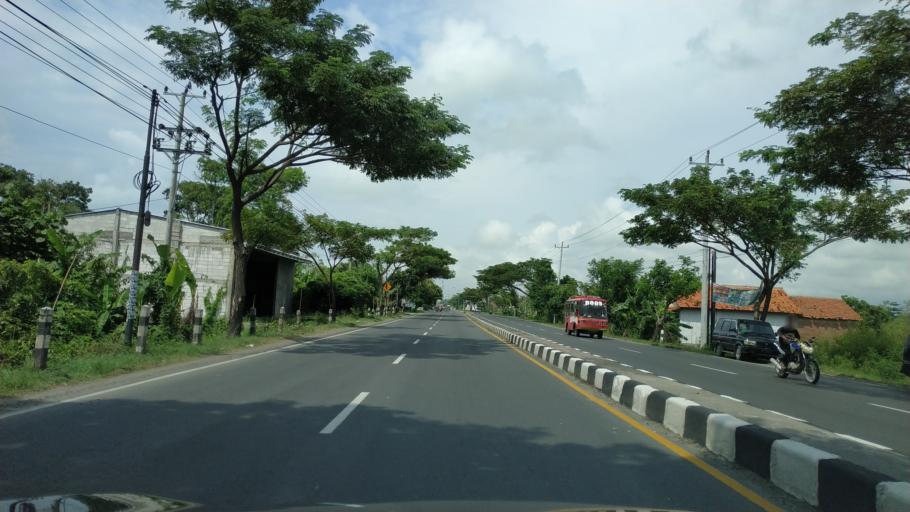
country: ID
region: Central Java
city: Tarub
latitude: -6.8727
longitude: 109.2483
